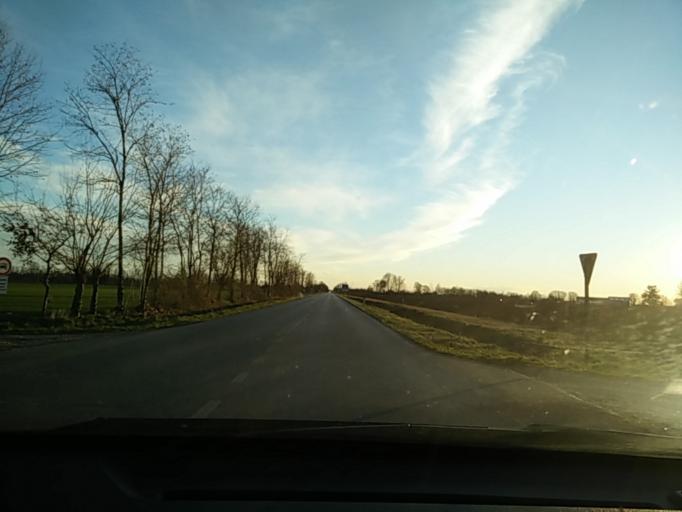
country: IT
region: Friuli Venezia Giulia
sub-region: Provincia di Udine
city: Talmassons
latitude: 45.9566
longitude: 13.0982
